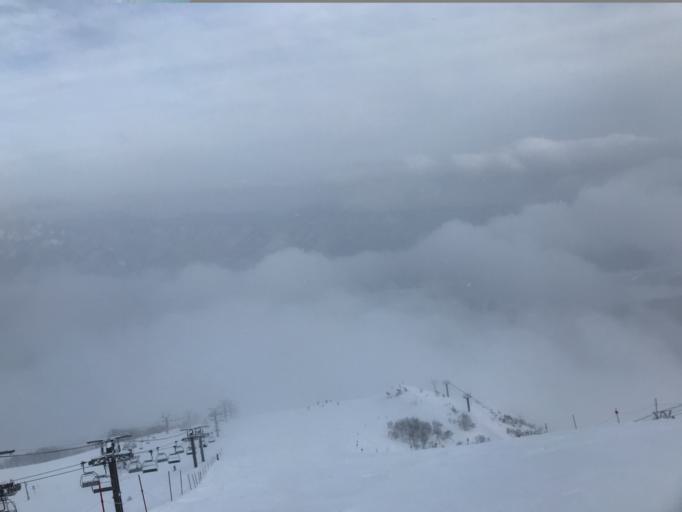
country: JP
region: Nagano
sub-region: Kitaazumi Gun
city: Hakuba
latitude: 36.6980
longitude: 137.8070
